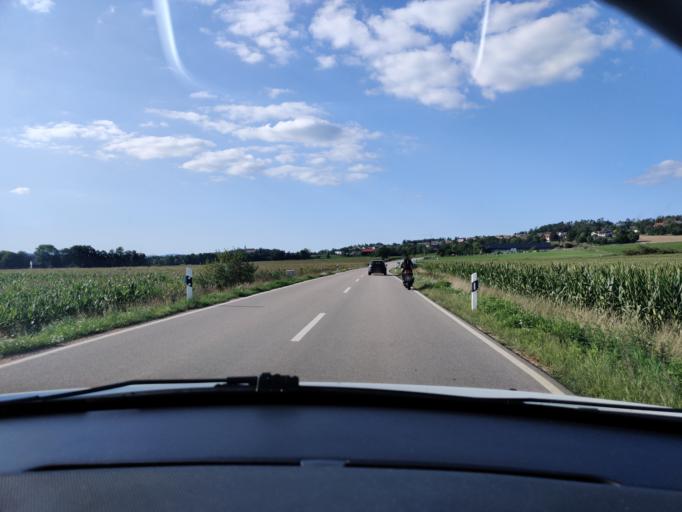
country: DE
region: Bavaria
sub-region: Upper Palatinate
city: Schwarzenfeld
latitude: 49.3781
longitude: 12.1574
